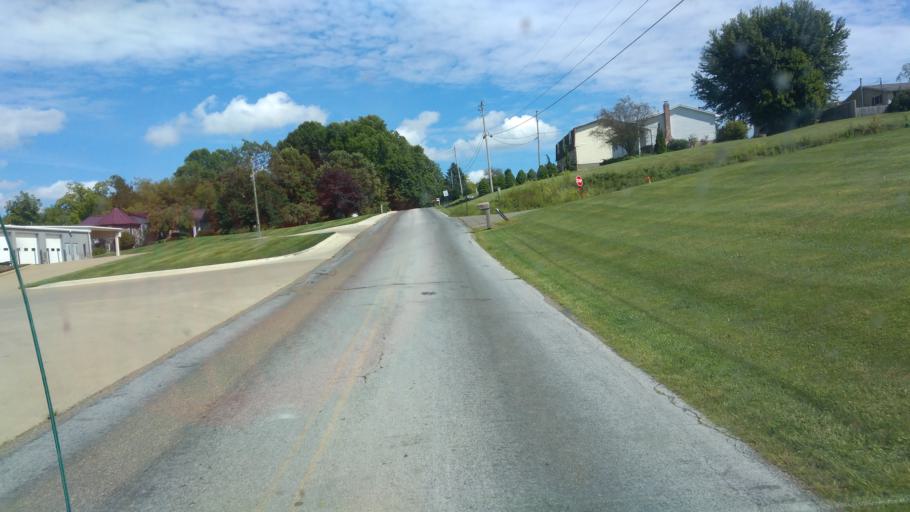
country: US
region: Ohio
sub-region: Holmes County
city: Millersburg
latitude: 40.5648
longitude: -81.8111
